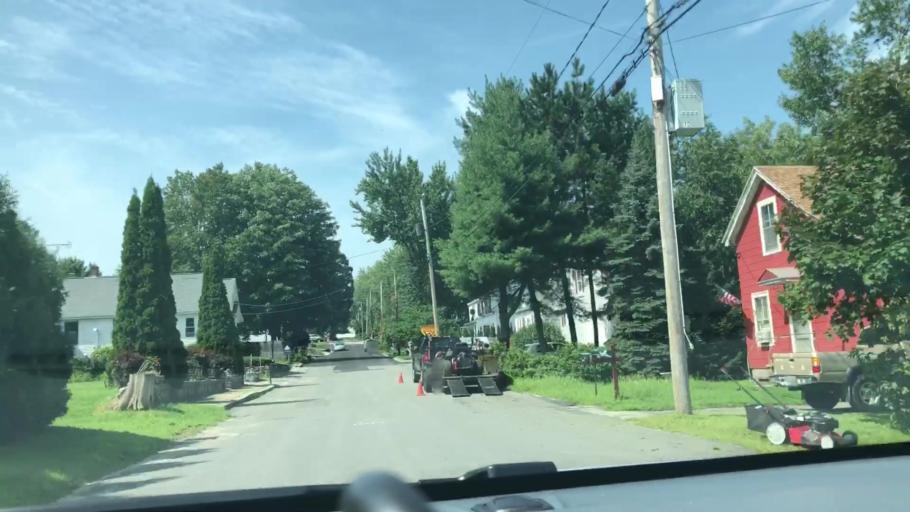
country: US
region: New Hampshire
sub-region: Hillsborough County
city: Pinardville
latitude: 42.9934
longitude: -71.5073
